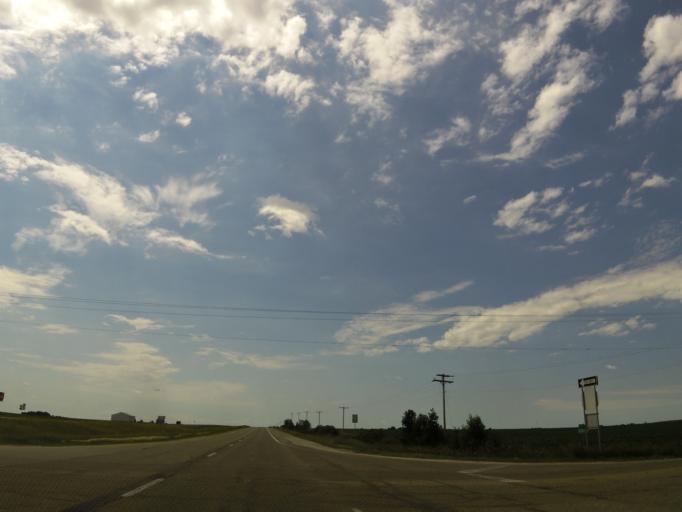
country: US
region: Iowa
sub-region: Bremer County
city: Tripoli
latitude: 42.7740
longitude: -92.3374
